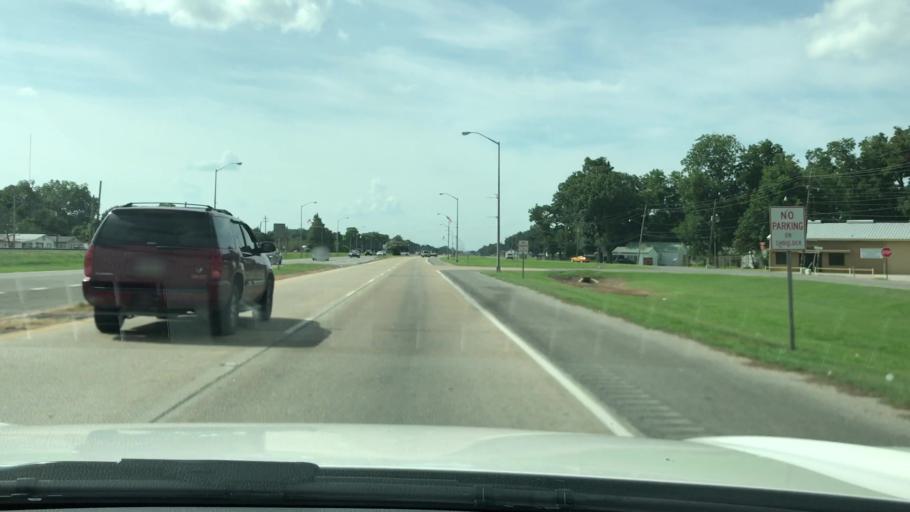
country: US
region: Louisiana
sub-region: Iberville Parish
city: Plaquemine
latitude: 30.2993
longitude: -91.2420
